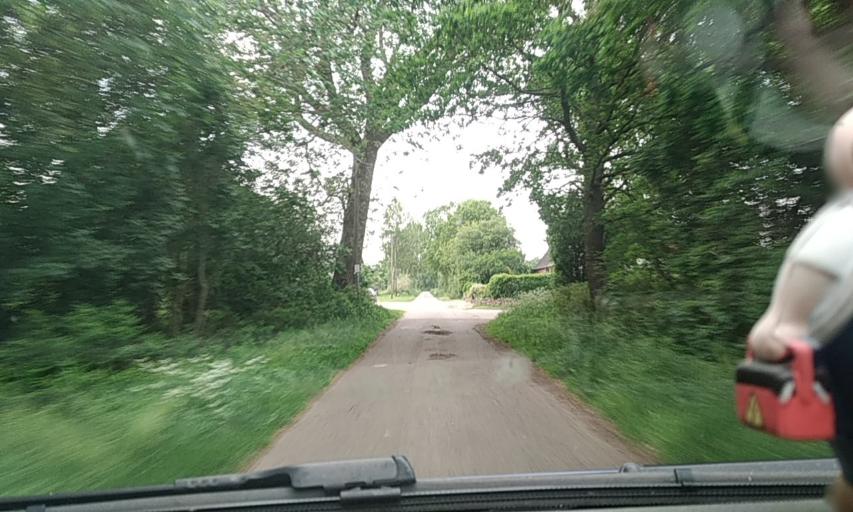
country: DE
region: Schleswig-Holstein
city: Borm
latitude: 54.3907
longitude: 9.3857
